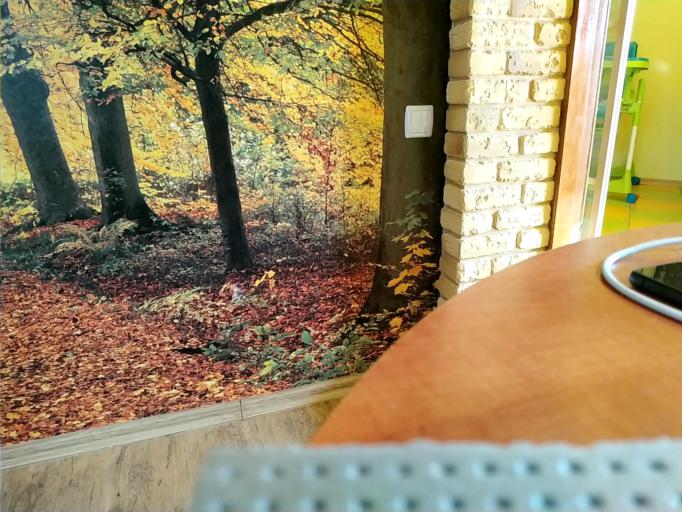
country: RU
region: Tverskaya
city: Kalashnikovo
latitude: 57.3462
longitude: 35.2216
